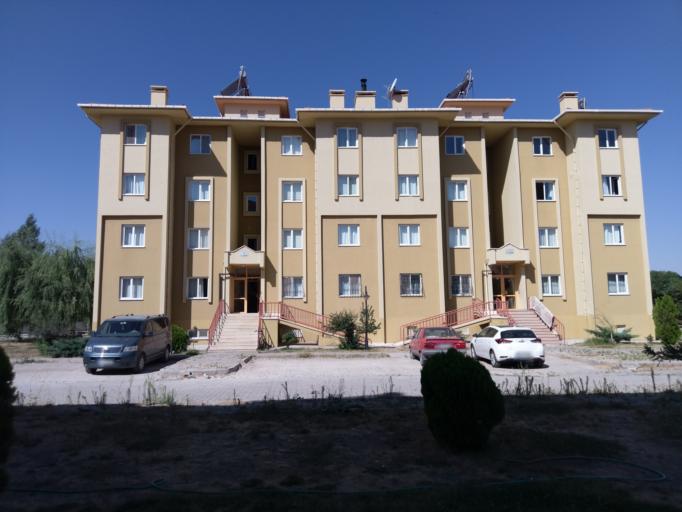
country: TR
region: Kayseri
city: Tomarza
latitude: 38.4583
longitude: 35.8066
